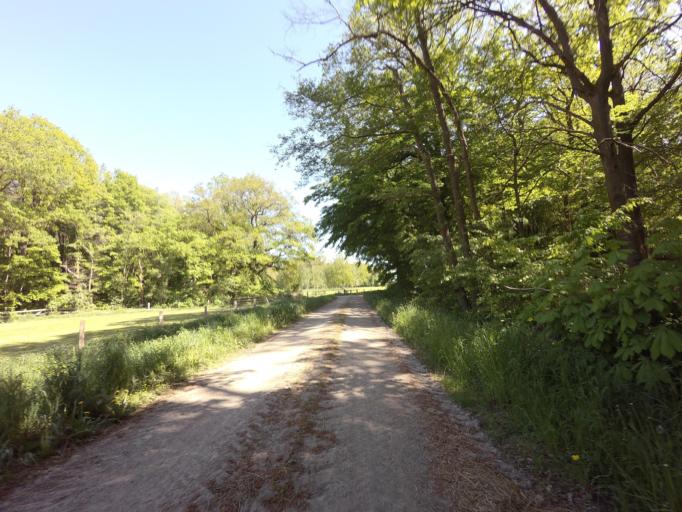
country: DE
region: Lower Saxony
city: Lehre
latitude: 52.3002
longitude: 10.6660
